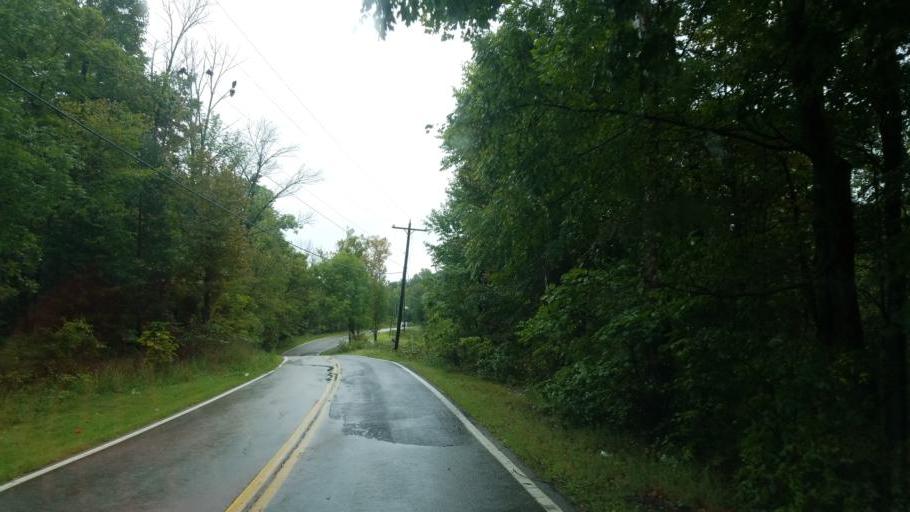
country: US
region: Ohio
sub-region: Adams County
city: West Union
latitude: 38.7921
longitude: -83.5440
